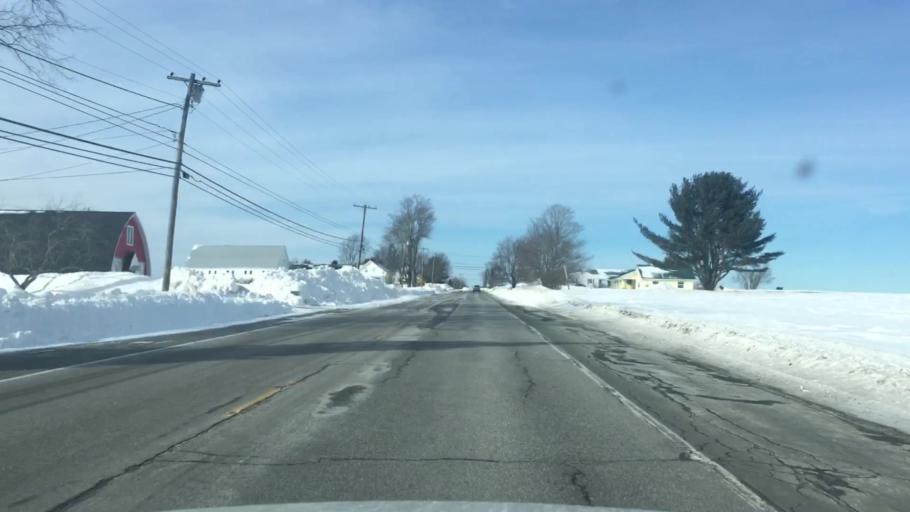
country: US
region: Maine
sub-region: Penobscot County
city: Charleston
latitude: 45.0238
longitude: -69.0297
